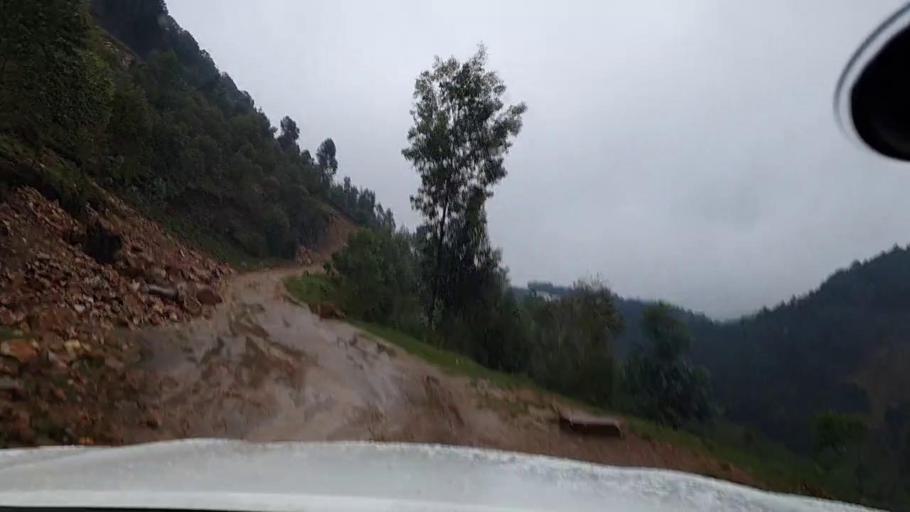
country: RW
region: Western Province
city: Kibuye
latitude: -2.1310
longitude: 29.4685
